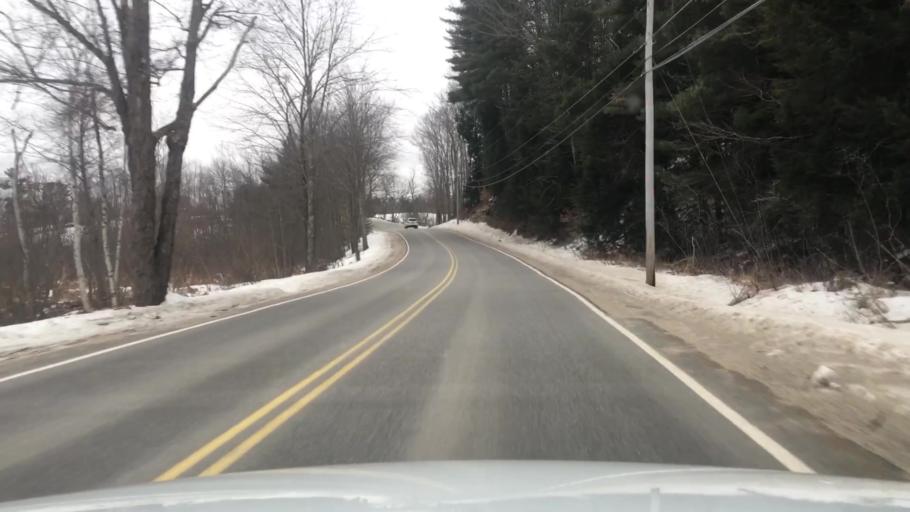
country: US
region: Maine
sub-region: York County
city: Springvale
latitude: 43.5022
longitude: -70.8149
